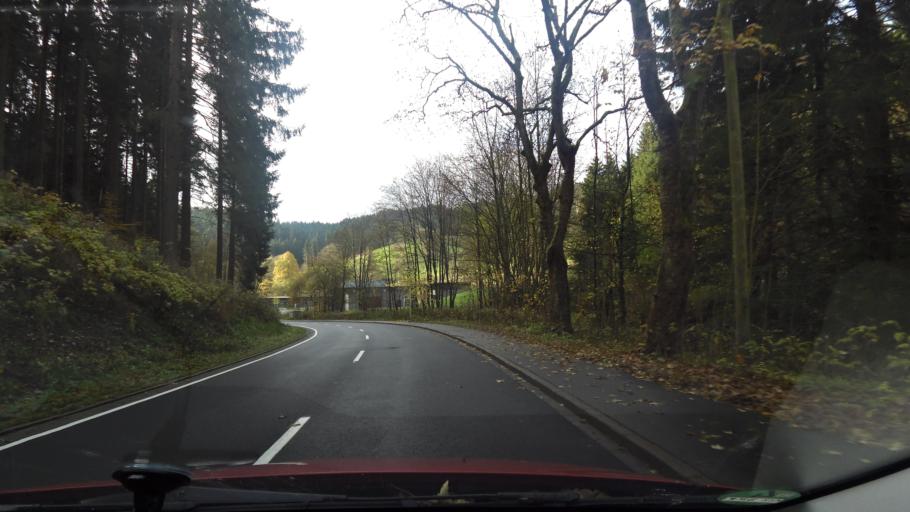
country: DE
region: Lower Saxony
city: Sankt Andreasberg
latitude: 51.7120
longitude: 10.5025
